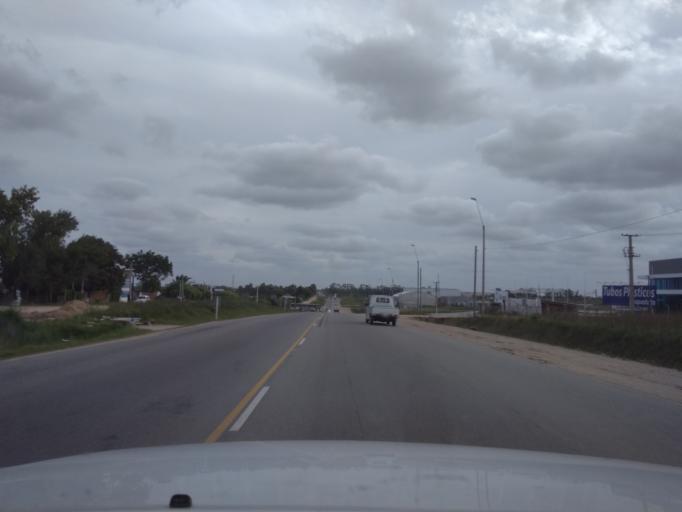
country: UY
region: Canelones
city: Colonia Nicolich
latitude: -34.7895
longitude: -56.0014
